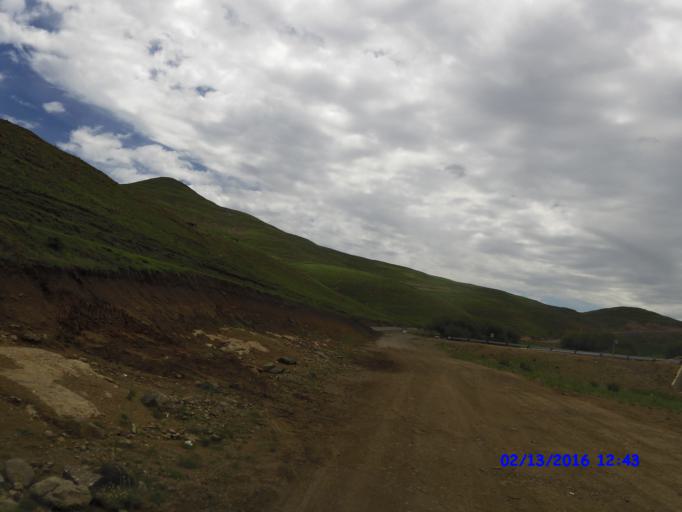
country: LS
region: Maseru
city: Nako
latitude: -29.8270
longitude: 28.0363
